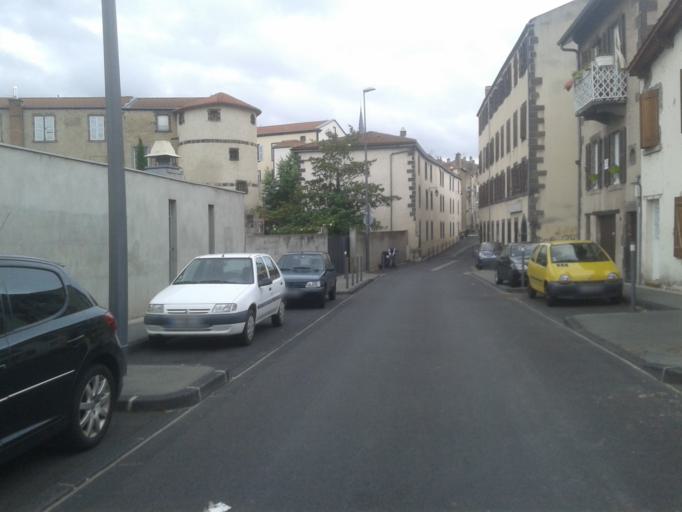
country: FR
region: Auvergne
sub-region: Departement du Puy-de-Dome
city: Clermont-Ferrand
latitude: 45.7848
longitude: 3.0811
